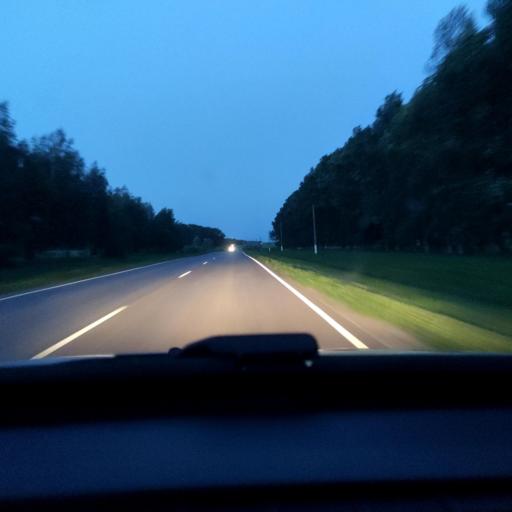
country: RU
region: Voronezj
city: Panino
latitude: 51.6587
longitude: 39.9925
